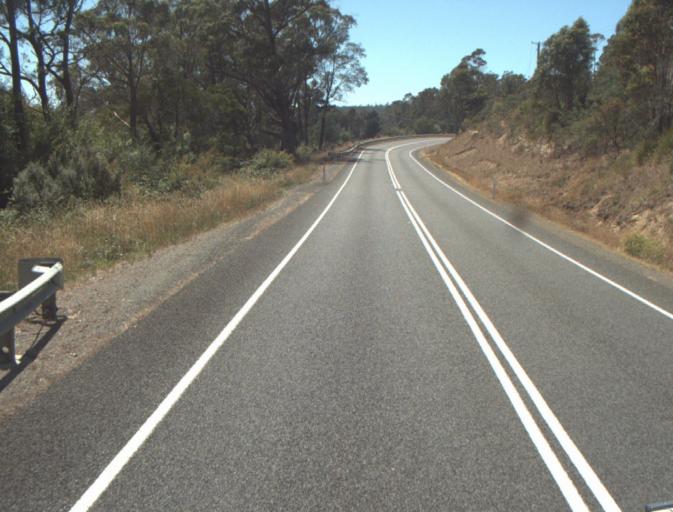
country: AU
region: Tasmania
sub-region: Launceston
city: Newstead
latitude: -41.3719
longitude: 147.3167
